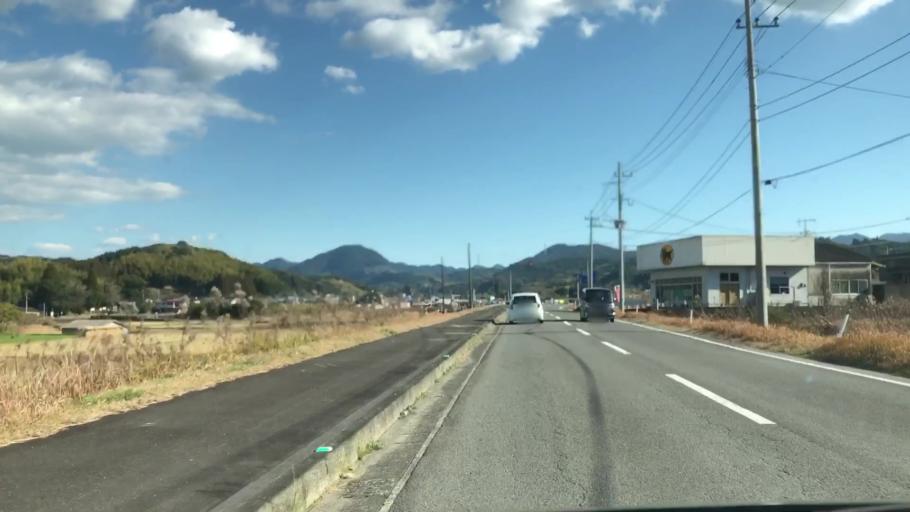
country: JP
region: Kagoshima
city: Satsumasendai
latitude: 31.7966
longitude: 130.4365
